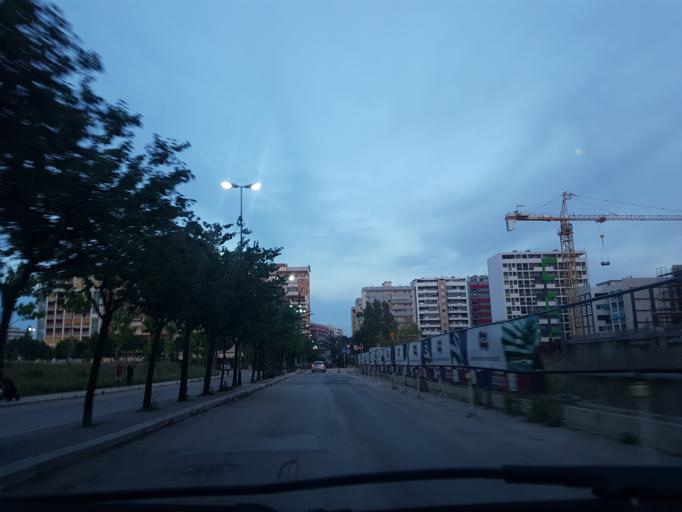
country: IT
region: Apulia
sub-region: Provincia di Barletta - Andria - Trani
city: Barletta
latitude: 41.3059
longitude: 16.2761
